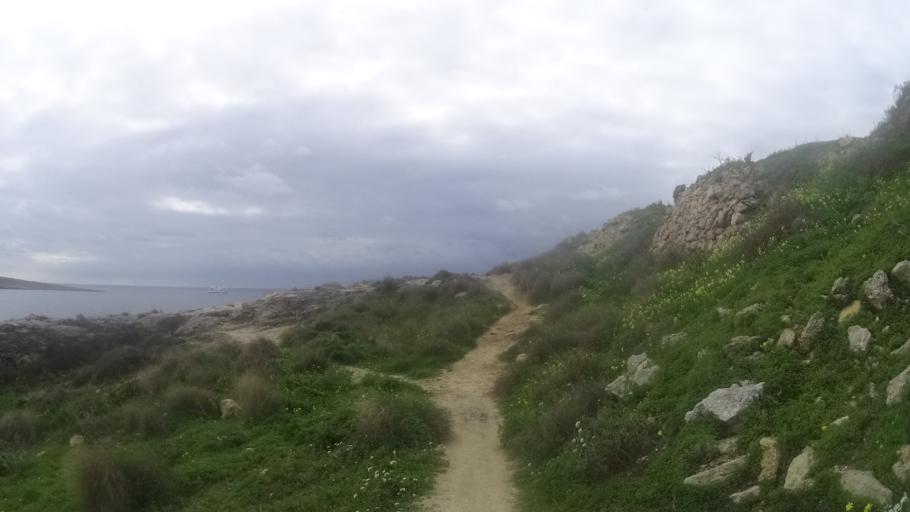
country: MT
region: Il-Qala
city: Qala
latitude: 36.0267
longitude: 14.3204
